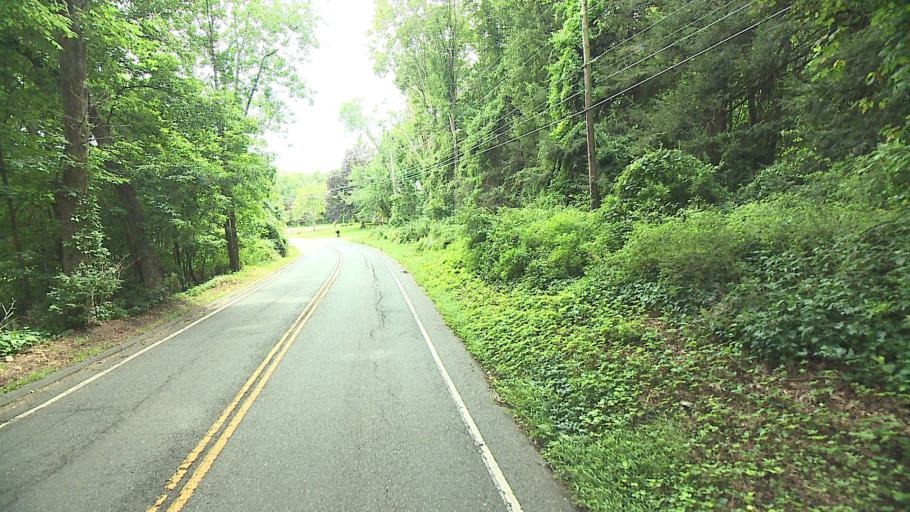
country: US
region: Connecticut
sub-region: Litchfield County
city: Woodbury
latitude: 41.5434
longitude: -73.2364
